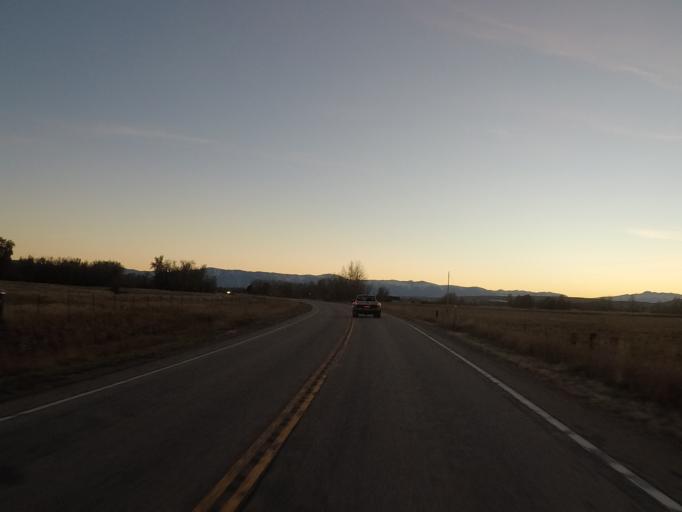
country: US
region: Montana
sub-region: Carbon County
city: Red Lodge
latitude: 45.3818
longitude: -109.1461
